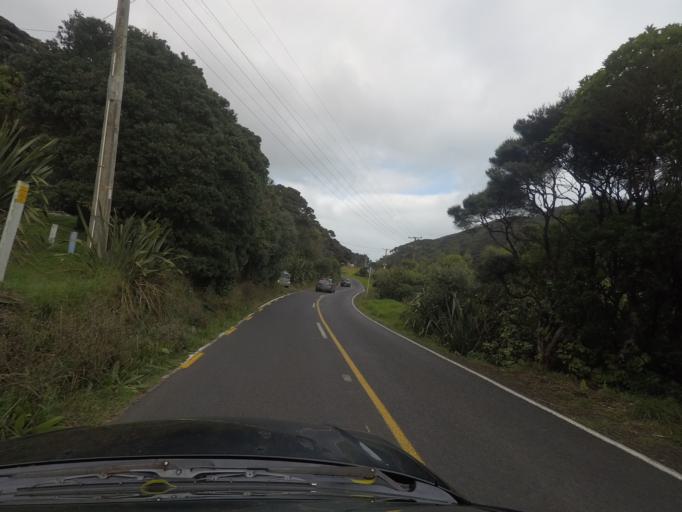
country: NZ
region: Auckland
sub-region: Auckland
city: Muriwai Beach
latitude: -36.8812
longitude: 174.4513
